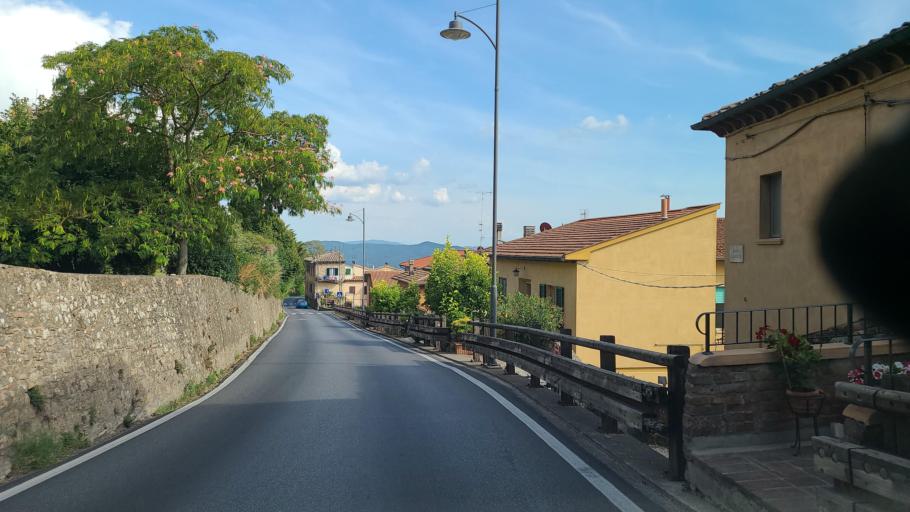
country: IT
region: Tuscany
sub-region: Province of Pisa
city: Volterra
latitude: 43.3991
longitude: 10.8723
